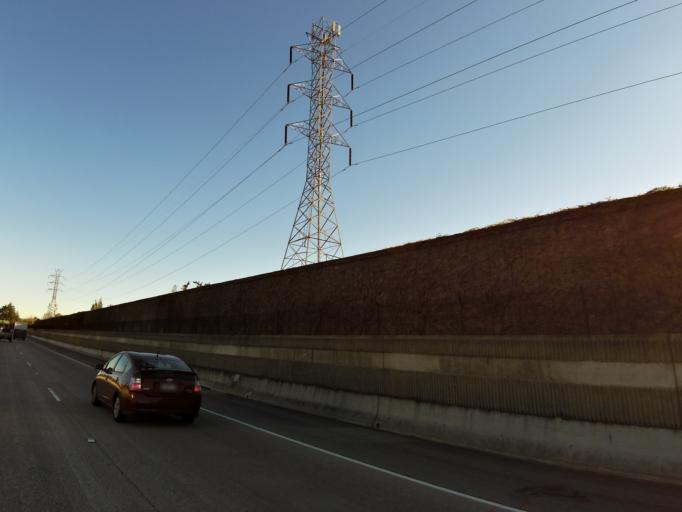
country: US
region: California
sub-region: Santa Clara County
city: Monte Sereno
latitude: 37.2618
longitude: -121.9738
